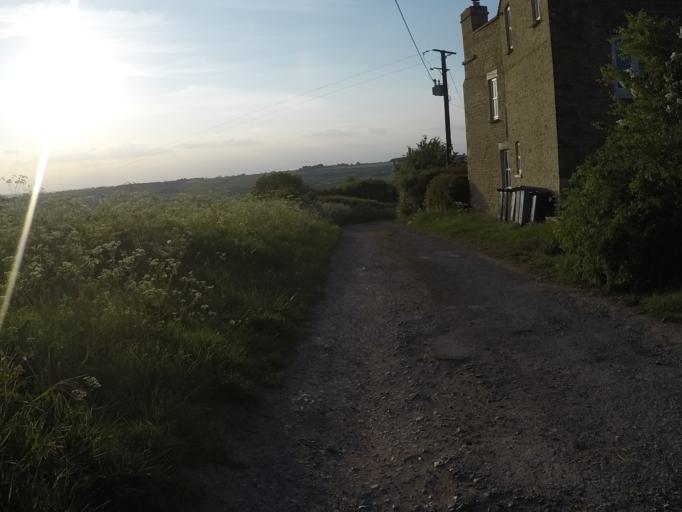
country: GB
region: England
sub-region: Oxfordshire
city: Charlbury
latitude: 51.8683
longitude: -1.5364
